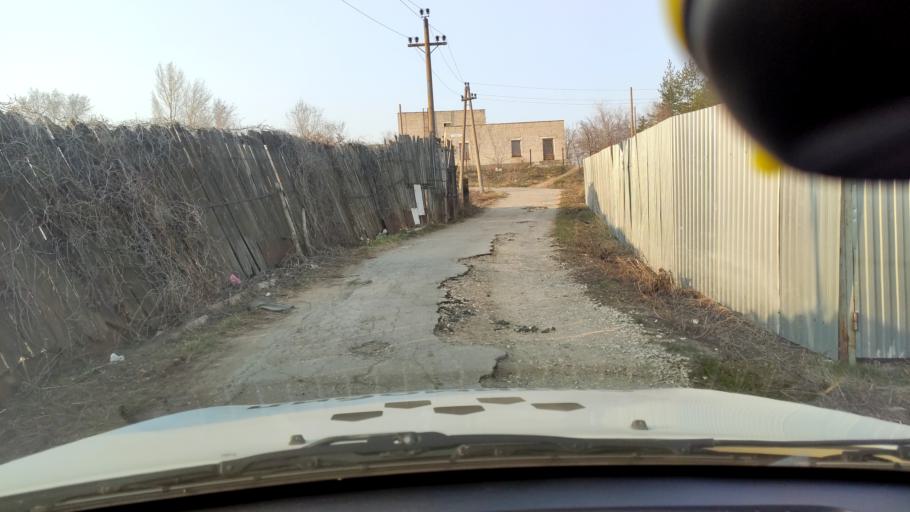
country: RU
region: Samara
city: Zhigulevsk
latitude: 53.4763
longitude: 49.5387
